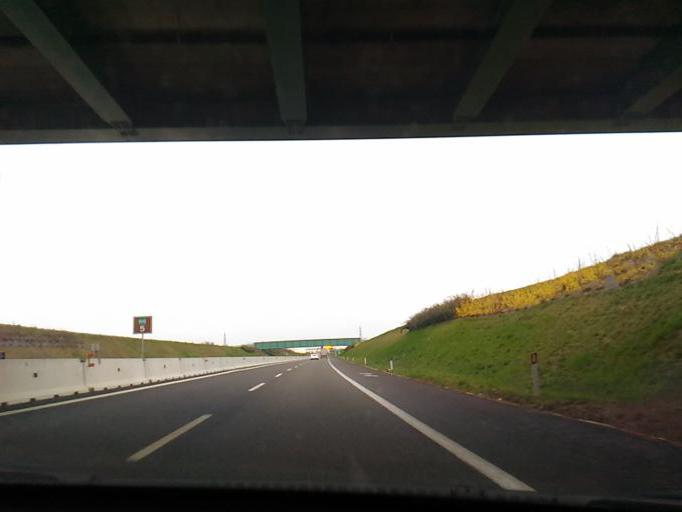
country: IT
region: Lombardy
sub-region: Provincia di Como
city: Limido Comasco
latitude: 45.6768
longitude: 8.9836
